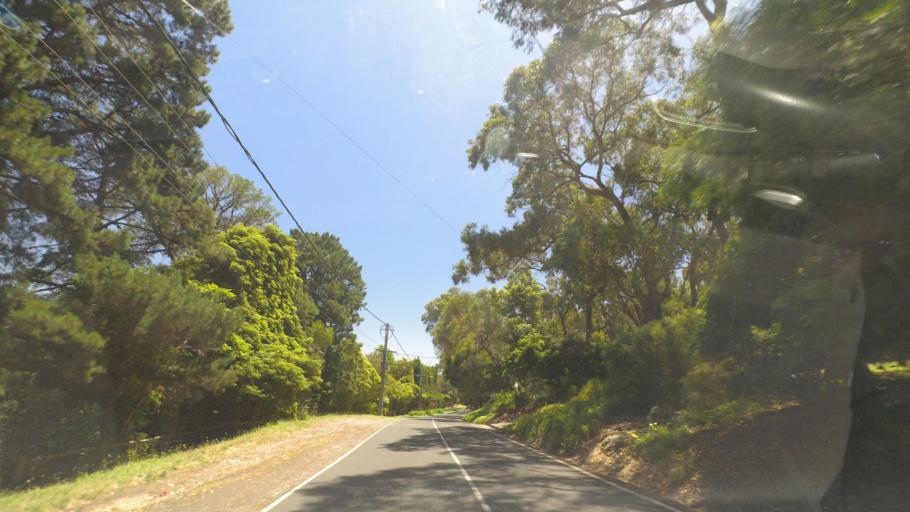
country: AU
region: Victoria
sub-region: Yarra Ranges
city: Montrose
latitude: -37.8204
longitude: 145.3415
